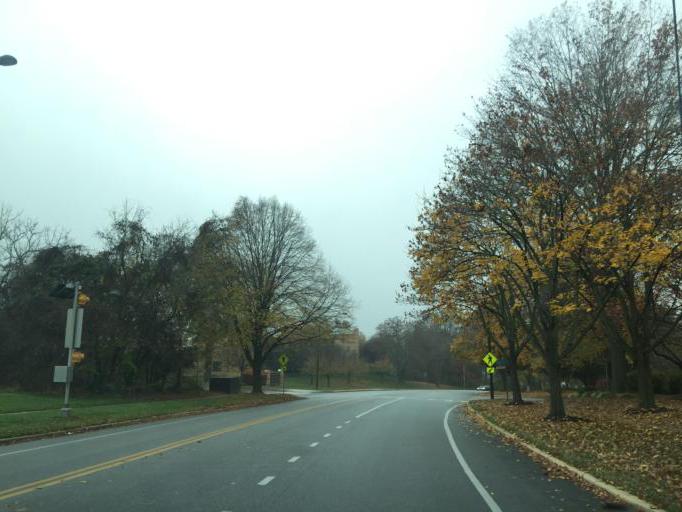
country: US
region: Maryland
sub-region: Howard County
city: Riverside
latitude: 39.1913
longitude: -76.8454
